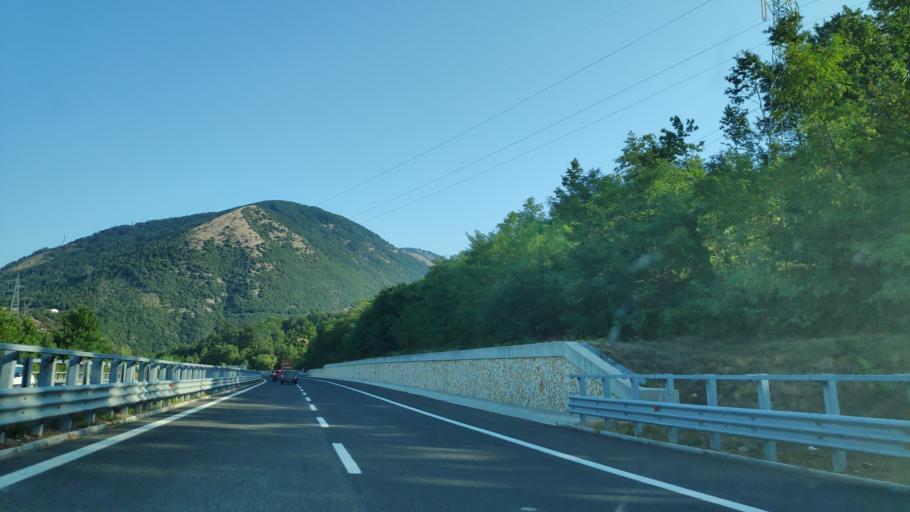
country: IT
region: Basilicate
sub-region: Provincia di Potenza
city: Lagonegro
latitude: 40.1190
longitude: 15.7844
